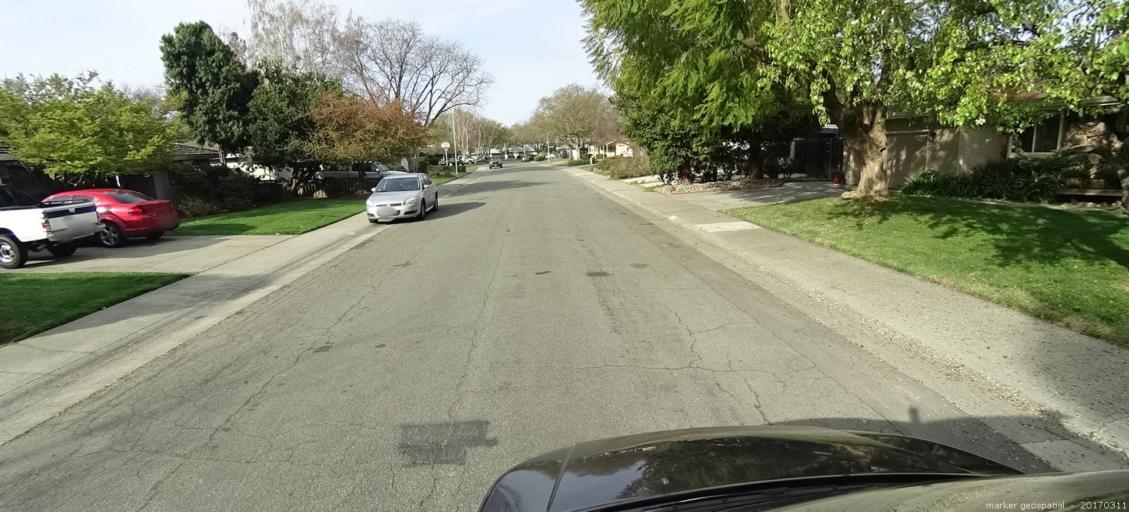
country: US
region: California
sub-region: Yolo County
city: West Sacramento
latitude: 38.5126
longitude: -121.5409
